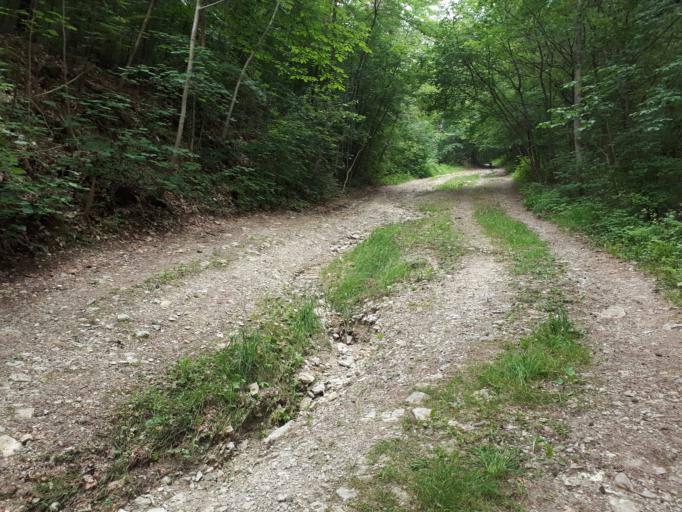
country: DE
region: Thuringia
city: Jena
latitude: 50.8882
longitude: 11.5696
